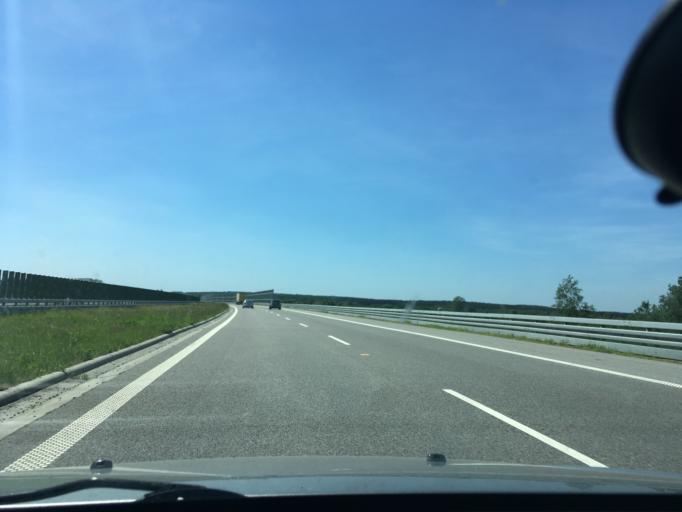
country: PL
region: Subcarpathian Voivodeship
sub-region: Powiat ropczycko-sedziszowski
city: Ostrow
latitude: 50.1075
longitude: 21.5942
